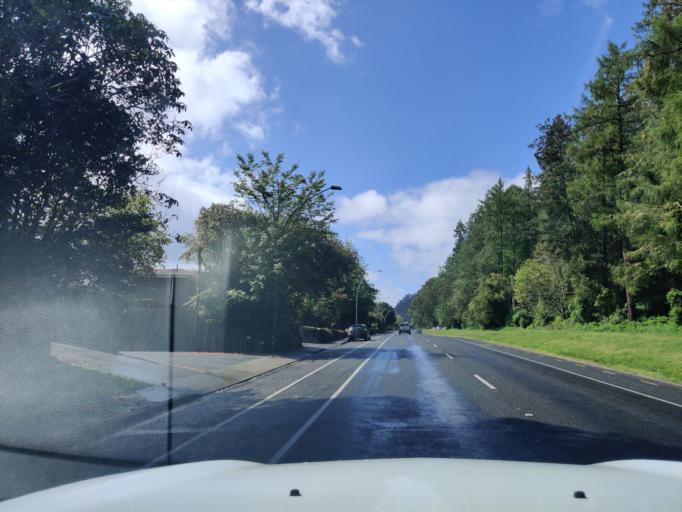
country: NZ
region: Bay of Plenty
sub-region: Rotorua District
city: Rotorua
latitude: -38.1520
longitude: 176.2844
